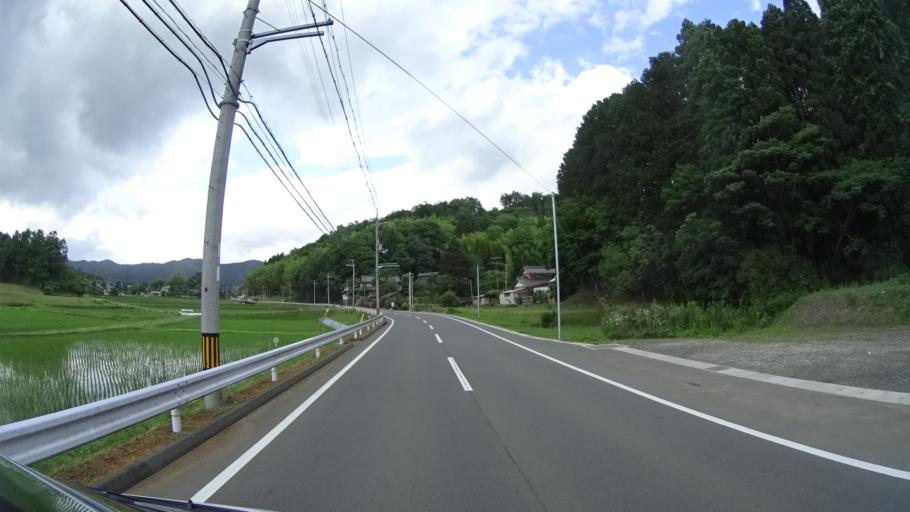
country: JP
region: Kyoto
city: Ayabe
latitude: 35.3374
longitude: 135.2038
